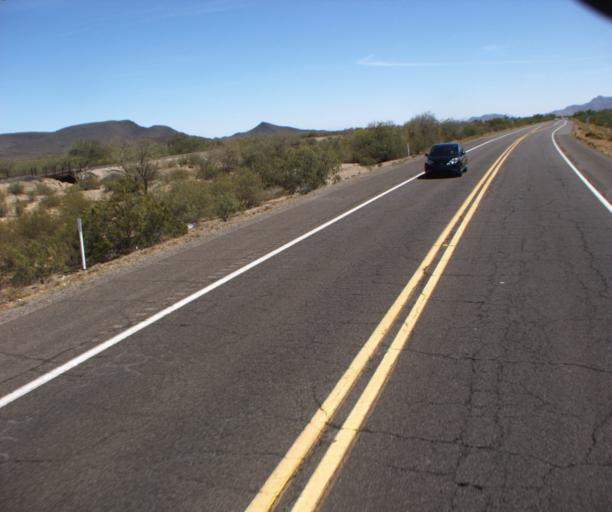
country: US
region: Arizona
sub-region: Pinal County
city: Sacaton
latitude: 33.1364
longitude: -111.7538
